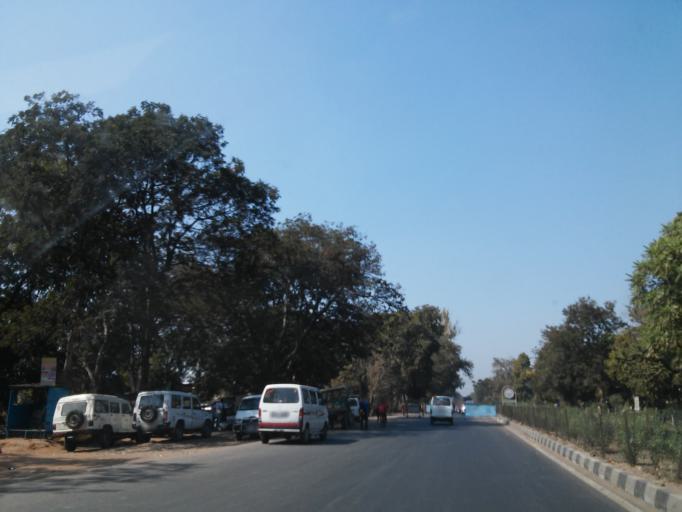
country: IN
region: Gujarat
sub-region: Gandhinagar
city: Ghandinagar
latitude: 23.2264
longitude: 72.7306
